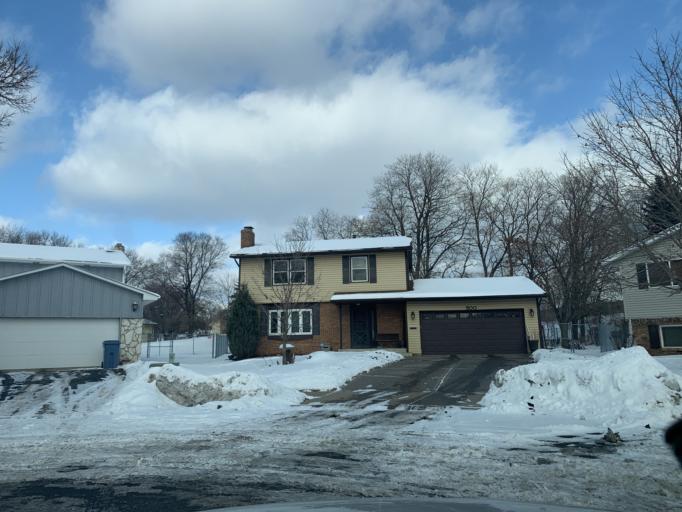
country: US
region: Minnesota
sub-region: Hennepin County
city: Minneapolis
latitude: 44.9949
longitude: -93.2854
